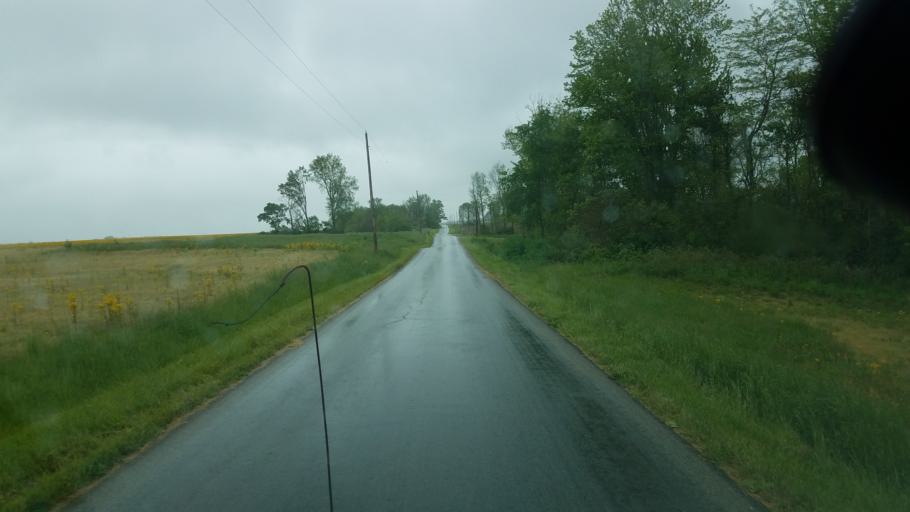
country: US
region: Ohio
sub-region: Highland County
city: Greenfield
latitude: 39.3246
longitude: -83.4251
